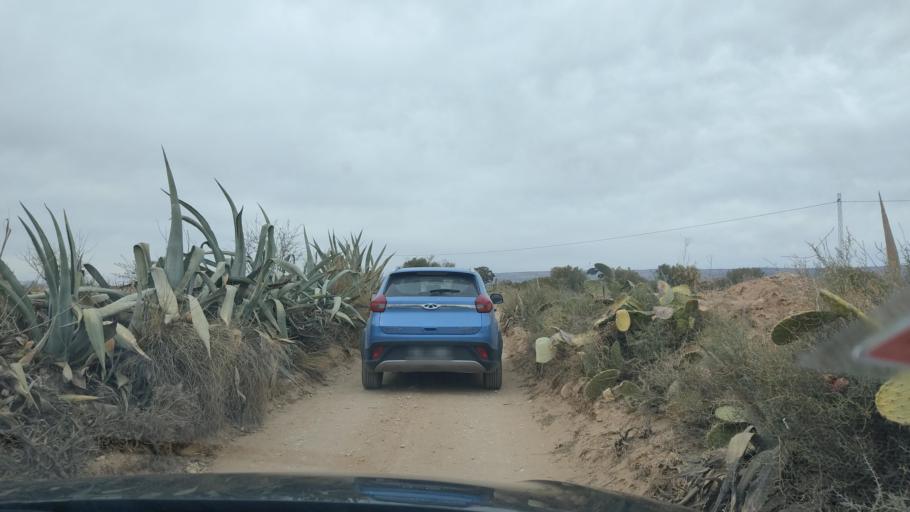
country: TN
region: Al Qasrayn
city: Kasserine
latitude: 35.2268
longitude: 8.9325
